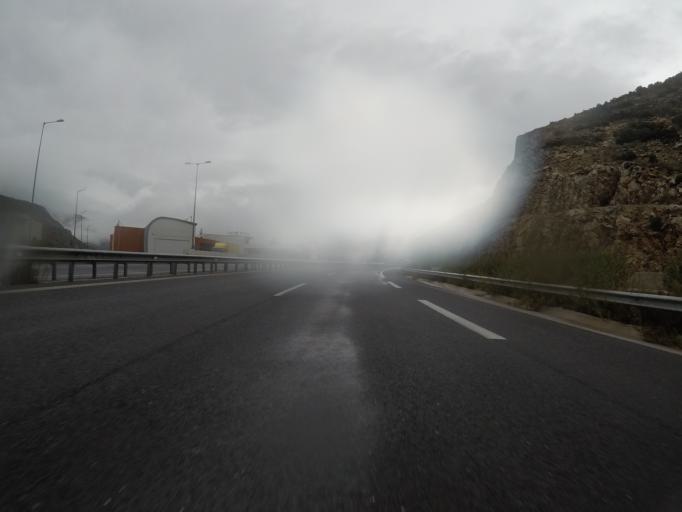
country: GR
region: Peloponnese
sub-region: Nomos Arkadias
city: Tripoli
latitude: 37.6499
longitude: 22.4654
